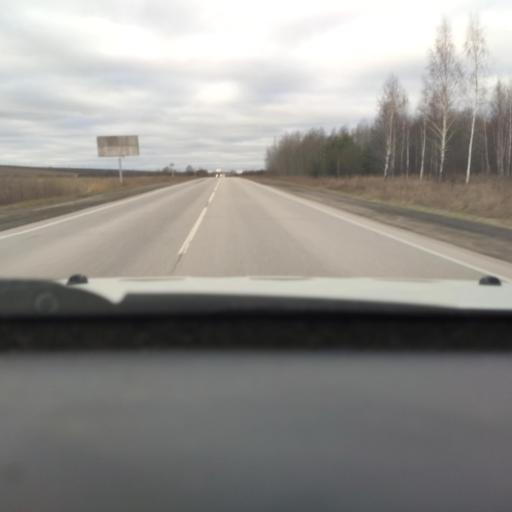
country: RU
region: Perm
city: Froly
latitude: 57.8982
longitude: 56.2387
